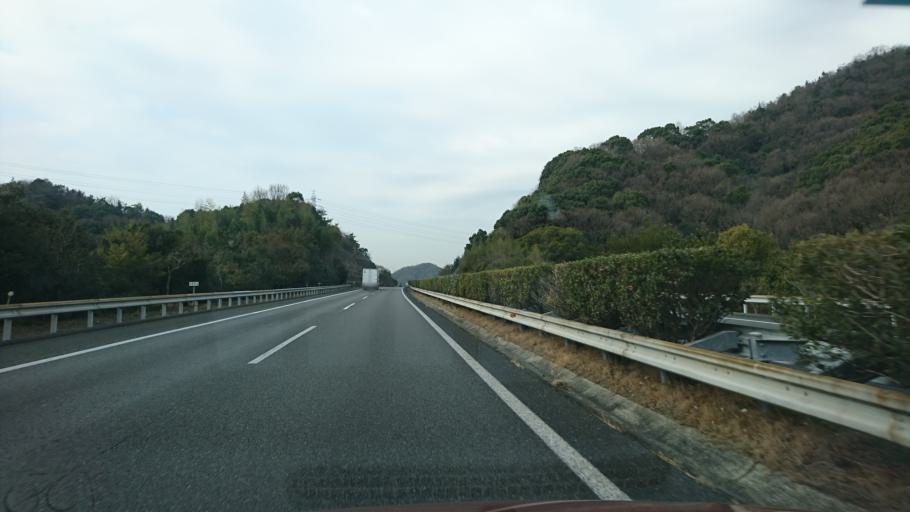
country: JP
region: Okayama
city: Kasaoka
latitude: 34.5321
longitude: 133.5422
